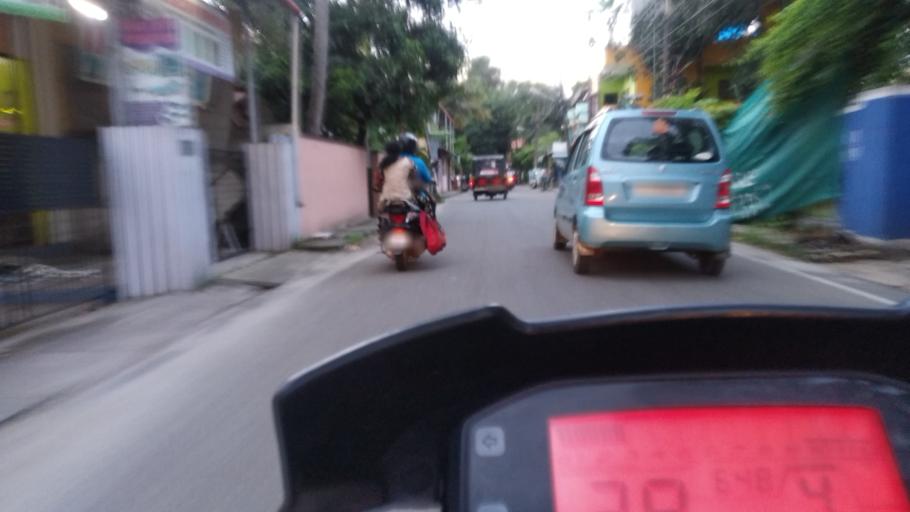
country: IN
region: Kerala
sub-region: Ernakulam
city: Elur
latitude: 10.0092
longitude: 76.2763
